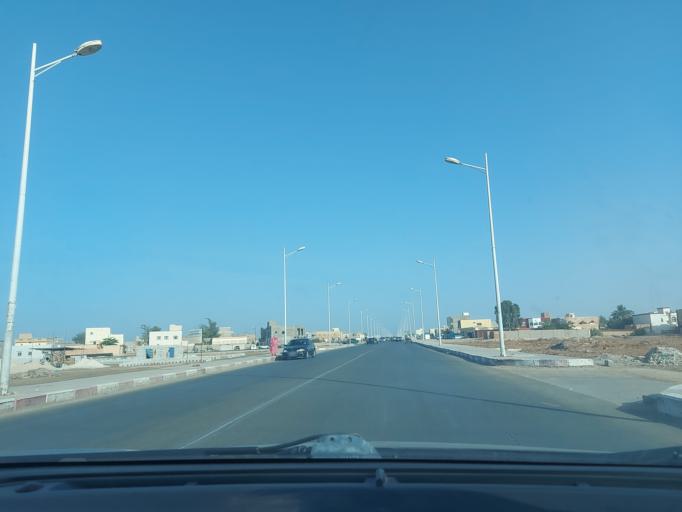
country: MR
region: Nouakchott
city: Nouakchott
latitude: 18.0858
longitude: -16.0019
